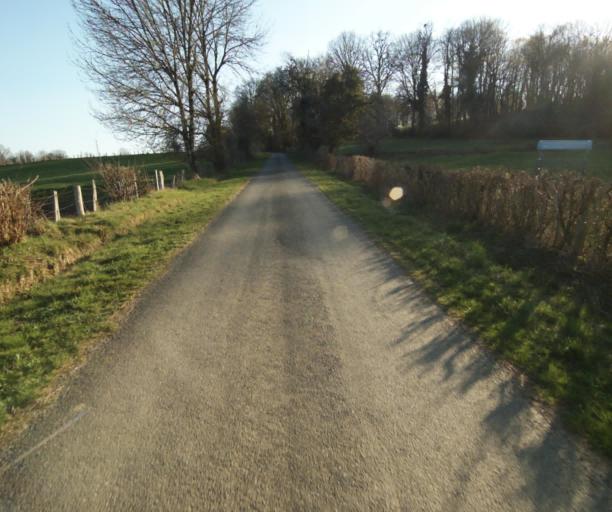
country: FR
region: Limousin
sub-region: Departement de la Correze
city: Saint-Clement
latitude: 45.3419
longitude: 1.6620
